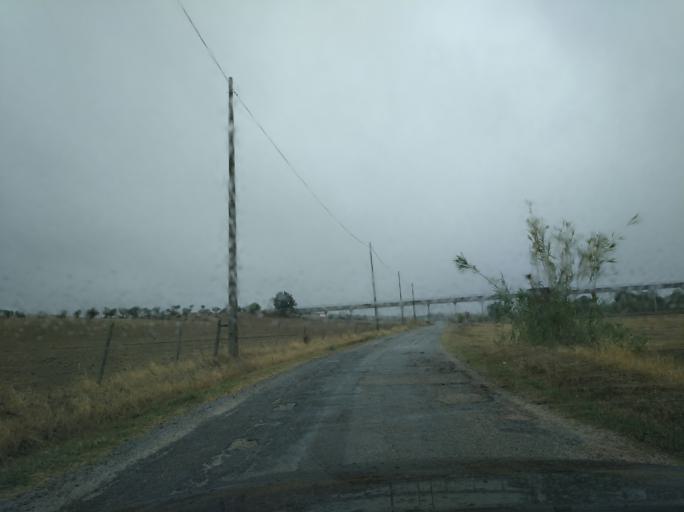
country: PT
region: Portalegre
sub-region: Campo Maior
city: Campo Maior
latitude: 38.9745
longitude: -7.0691
